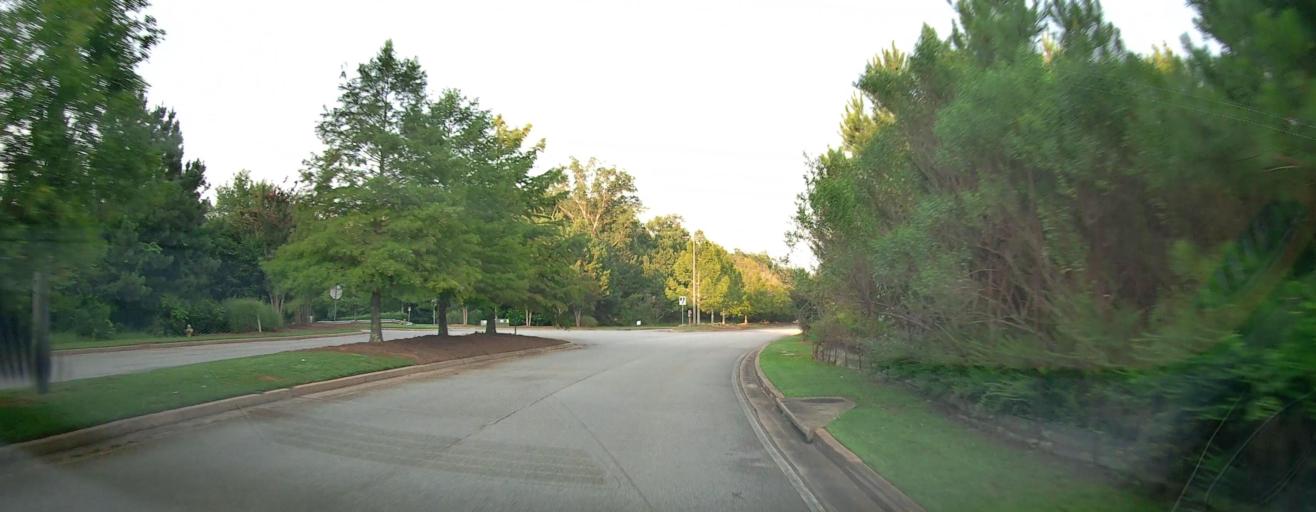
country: US
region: Georgia
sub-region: Bibb County
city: Macon
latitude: 32.9376
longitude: -83.7375
